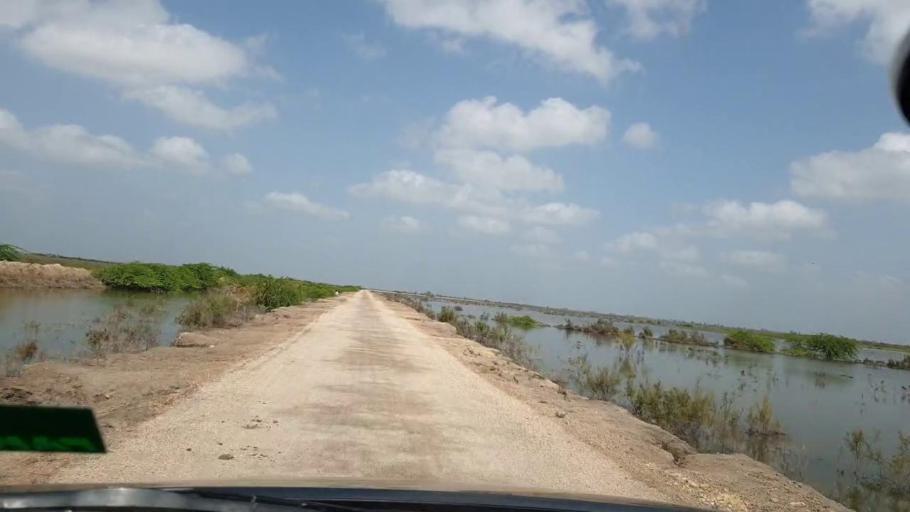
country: PK
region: Sindh
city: Kadhan
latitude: 24.5773
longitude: 69.1430
